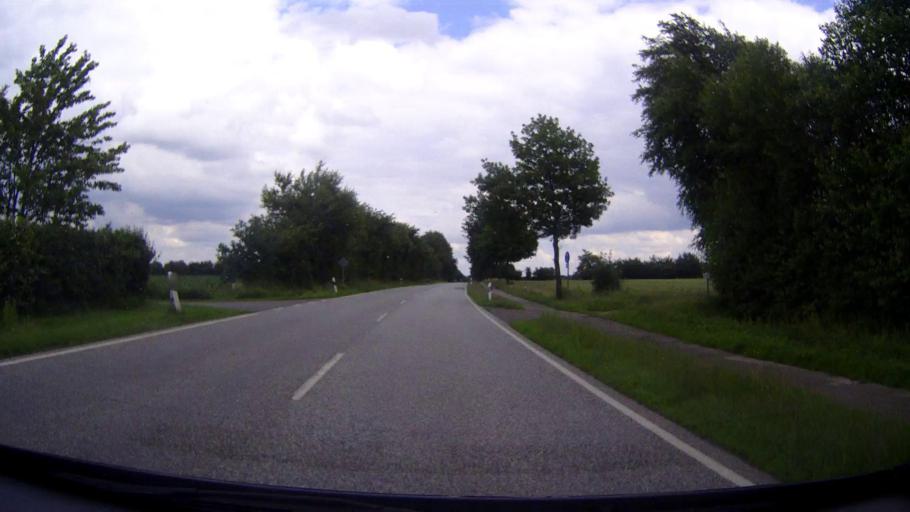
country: DE
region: Schleswig-Holstein
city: Beldorf
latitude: 54.1224
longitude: 9.3675
